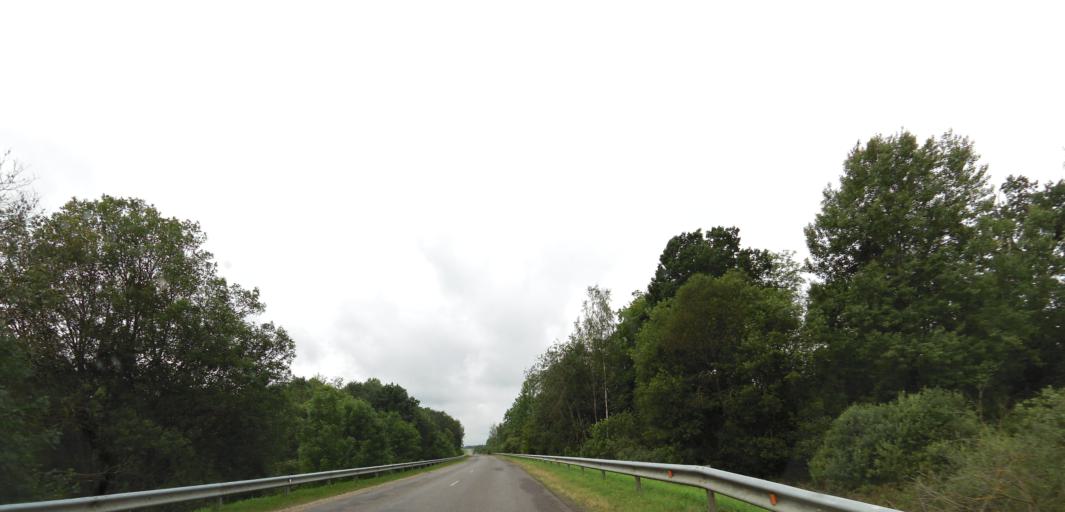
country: LT
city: Moletai
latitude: 55.2191
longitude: 25.2199
